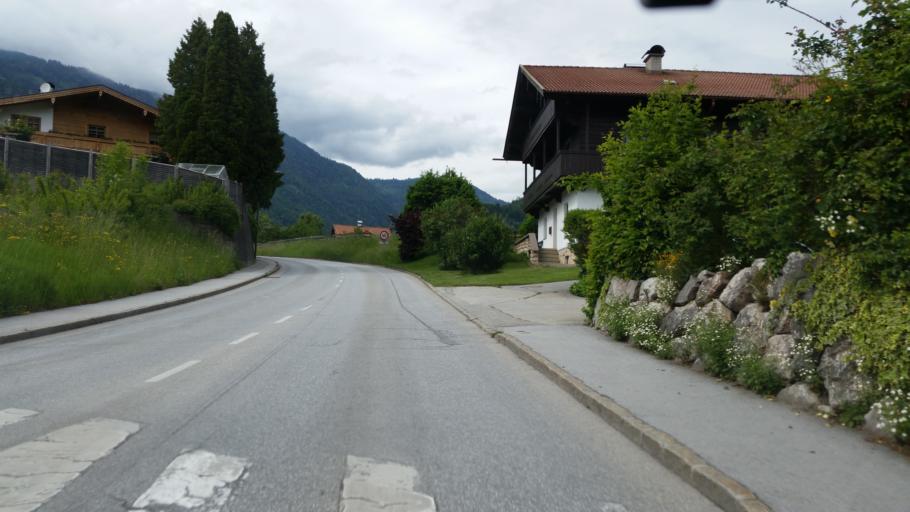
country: AT
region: Tyrol
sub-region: Politischer Bezirk Kufstein
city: Kramsach
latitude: 47.4431
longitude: 11.8769
